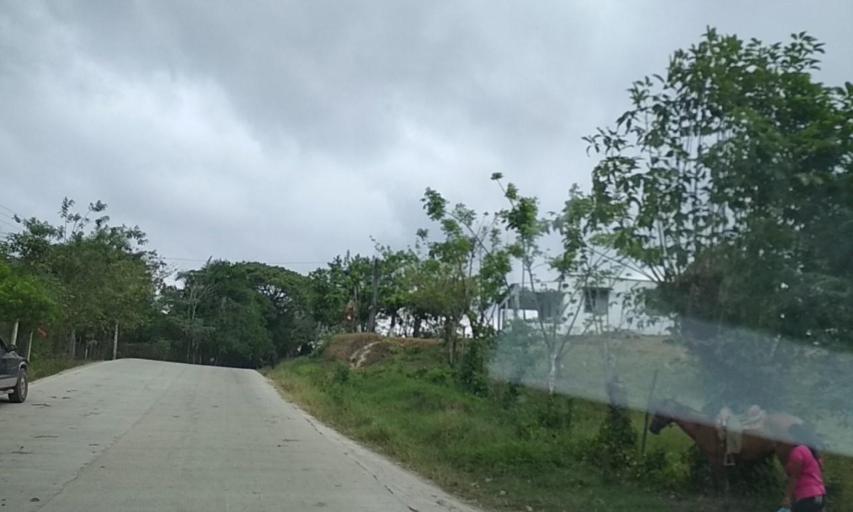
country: MX
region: Tabasco
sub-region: Huimanguillo
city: Francisco Rueda
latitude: 17.6534
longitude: -94.0923
